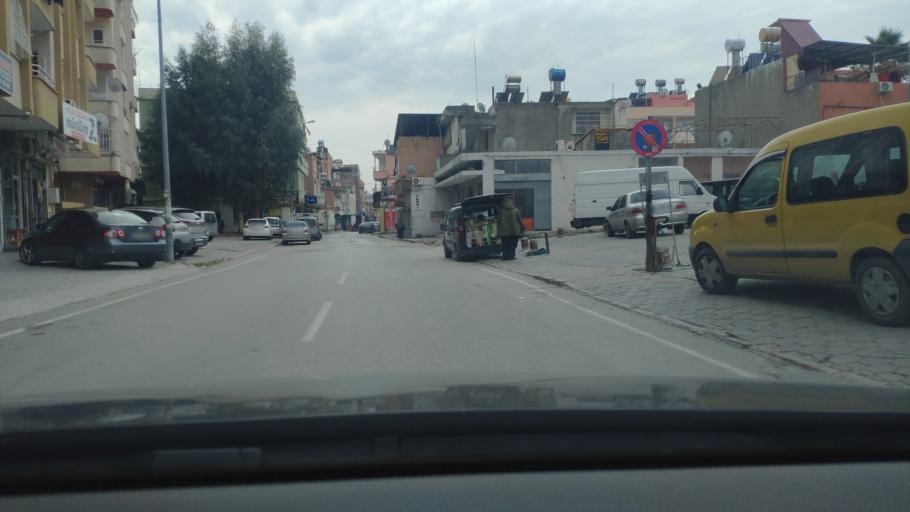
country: TR
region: Adana
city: Adana
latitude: 37.0184
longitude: 35.3142
